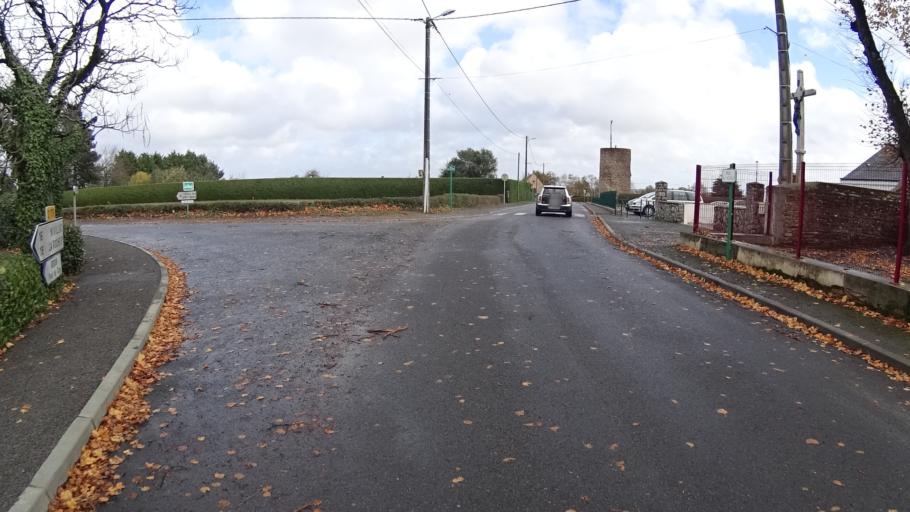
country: FR
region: Brittany
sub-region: Departement du Morbihan
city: Rieux
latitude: 47.5709
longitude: -2.1105
